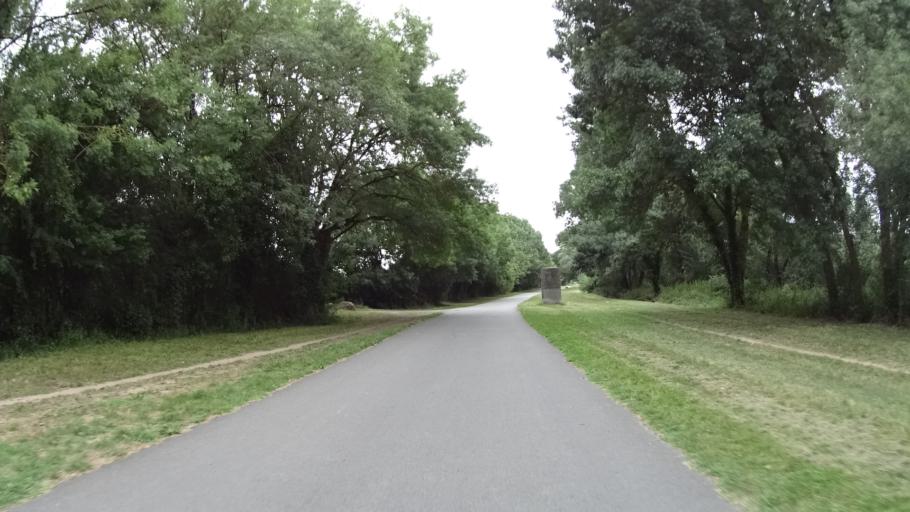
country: FR
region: Pays de la Loire
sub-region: Departement de la Loire-Atlantique
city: Thouare-sur-Loire
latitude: 47.2534
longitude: -1.4474
